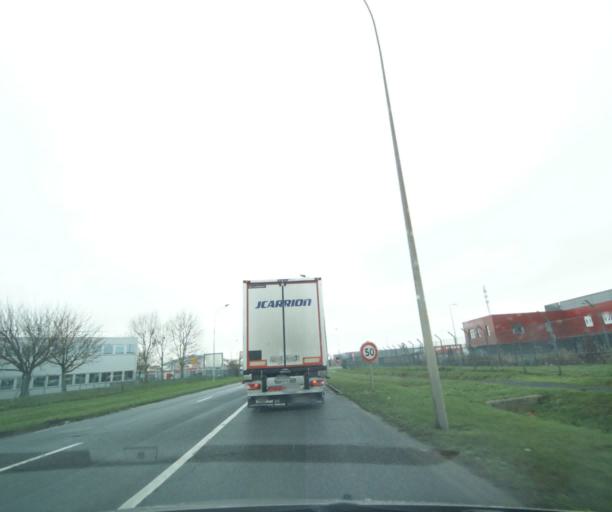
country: FR
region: Ile-de-France
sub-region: Departement du Val-de-Marne
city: Villeneuve-le-Roi
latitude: 48.7229
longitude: 2.4058
